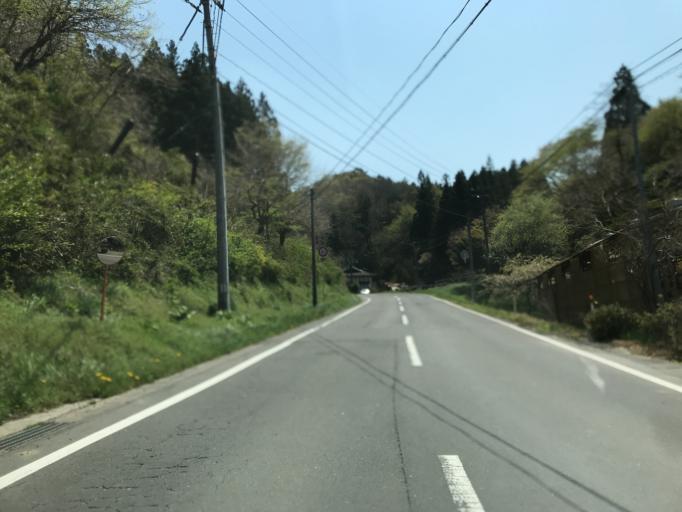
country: JP
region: Fukushima
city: Ishikawa
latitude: 37.0661
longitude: 140.4455
